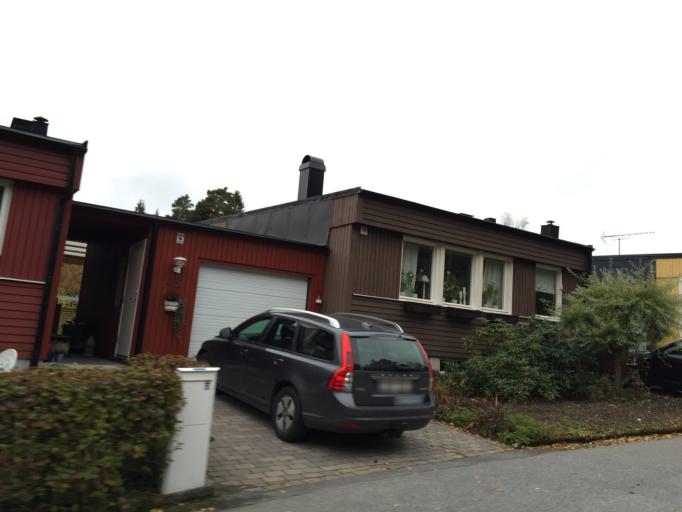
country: SE
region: Stockholm
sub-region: Salems Kommun
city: Ronninge
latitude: 59.2028
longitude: 17.7332
